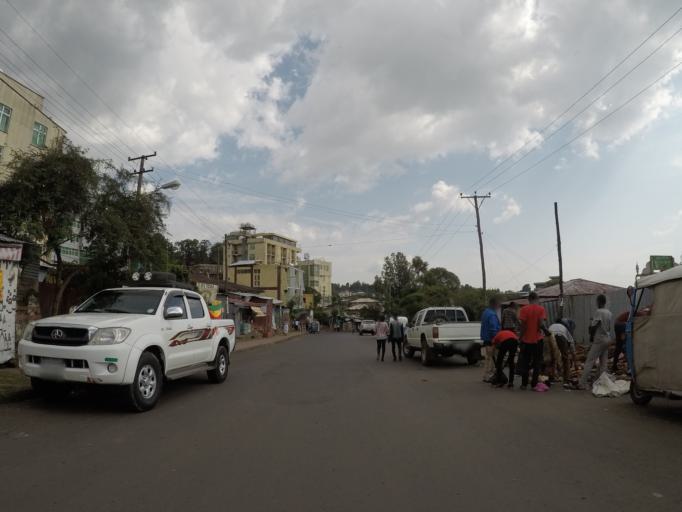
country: ET
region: Amhara
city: Gondar
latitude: 12.6151
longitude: 37.4697
